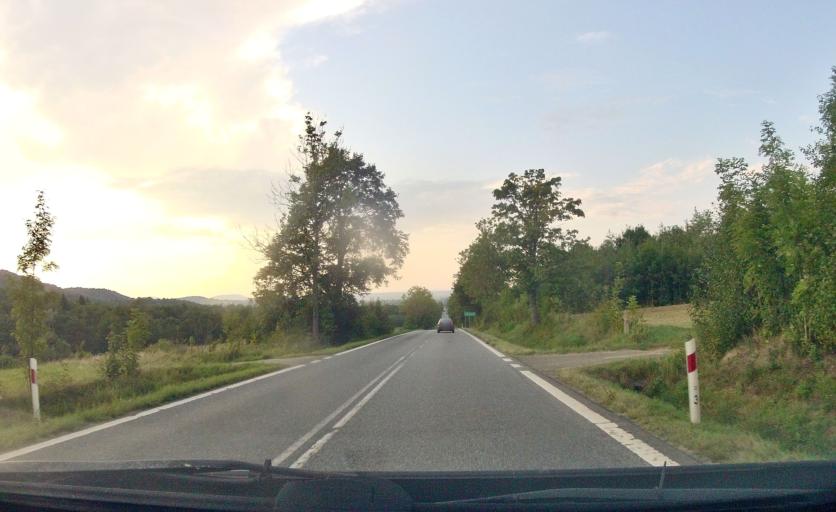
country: PL
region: Subcarpathian Voivodeship
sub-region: Powiat jasielski
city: Nowy Zmigrod
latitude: 49.5808
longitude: 21.5532
